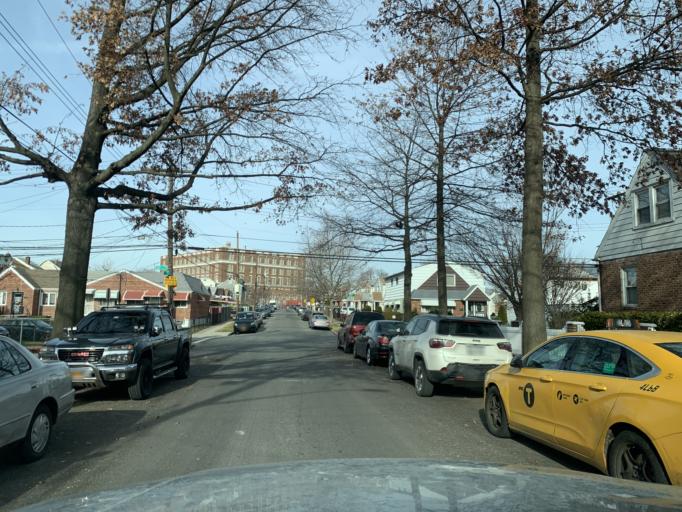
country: US
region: New York
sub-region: Queens County
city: Jamaica
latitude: 40.6989
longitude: -73.7800
